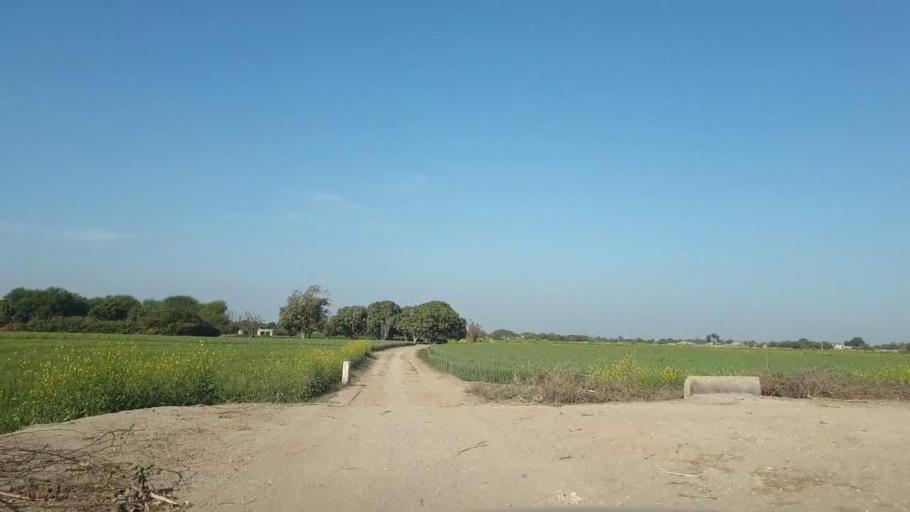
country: PK
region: Sindh
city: Tando Adam
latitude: 25.6803
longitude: 68.6881
